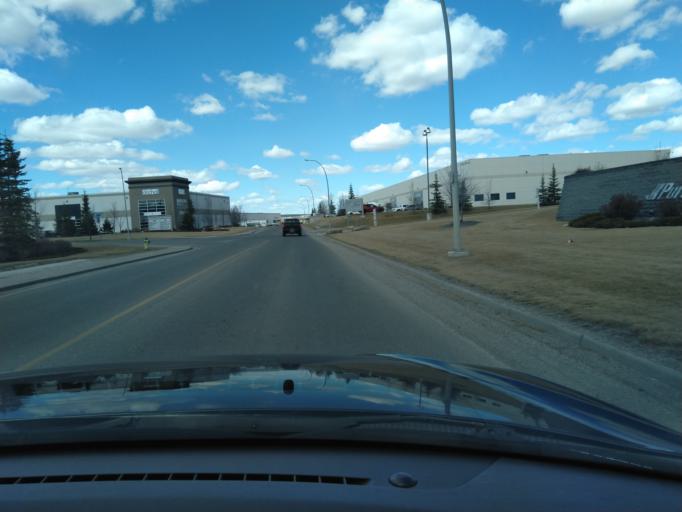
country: CA
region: Alberta
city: Calgary
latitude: 51.1211
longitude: -114.0359
